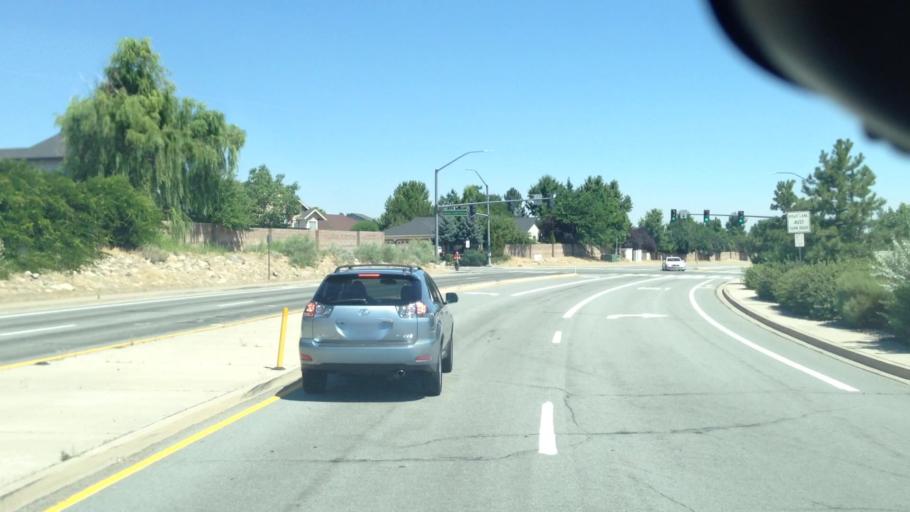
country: US
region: Nevada
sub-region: Washoe County
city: Sparks
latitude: 39.3937
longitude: -119.7680
